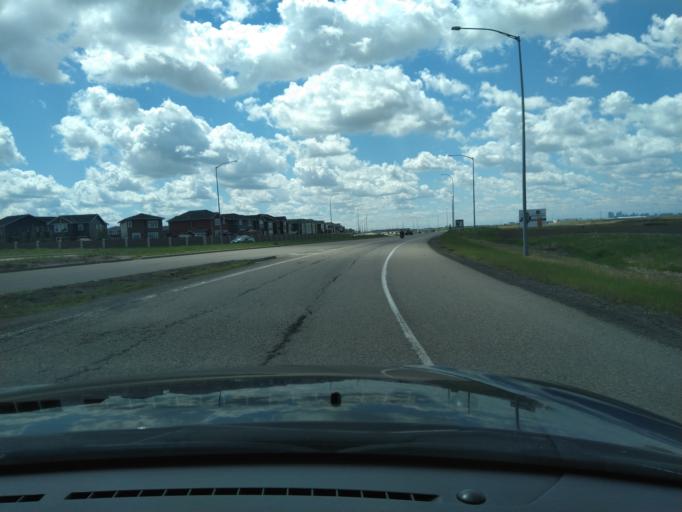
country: CA
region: Alberta
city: Airdrie
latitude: 51.1717
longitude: -113.9695
